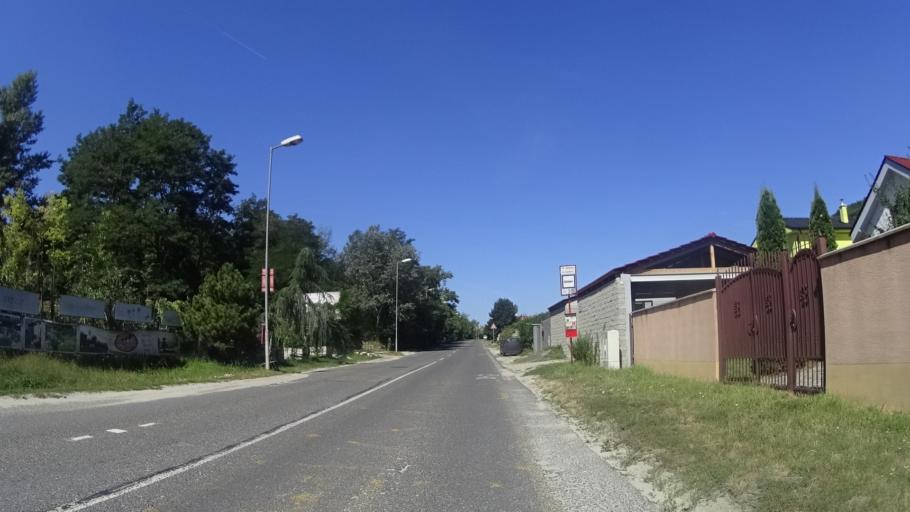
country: AT
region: Lower Austria
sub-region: Politischer Bezirk Bruck an der Leitha
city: Wolfsthal
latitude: 48.1569
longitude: 17.0140
